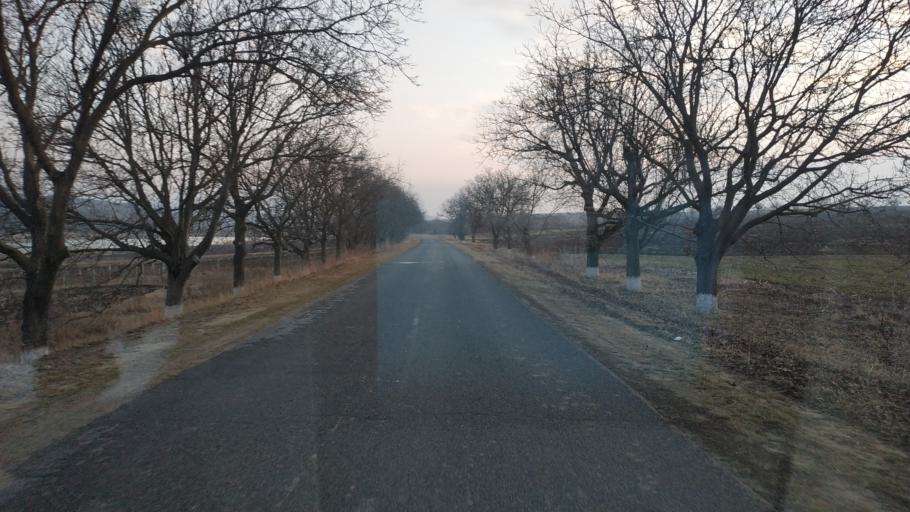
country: MD
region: Hincesti
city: Dancu
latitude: 46.7013
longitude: 28.3379
